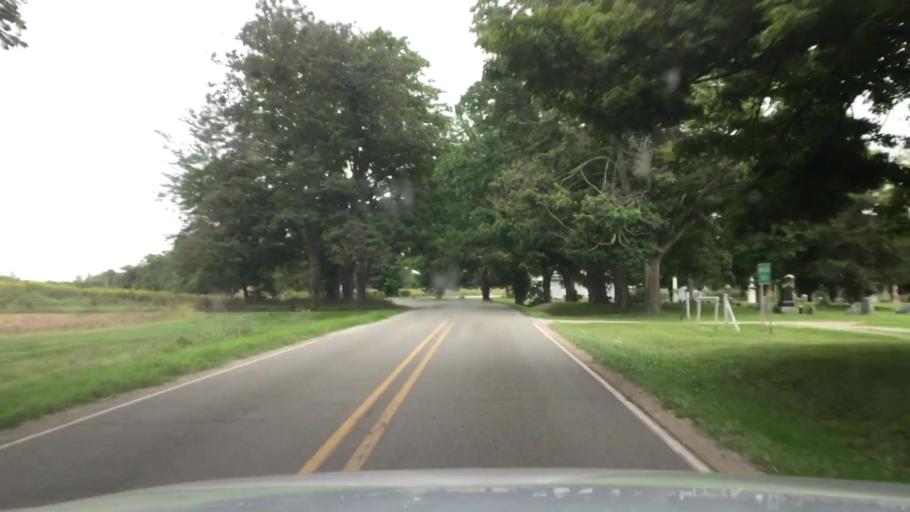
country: US
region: Michigan
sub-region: Shiawassee County
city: Durand
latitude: 42.8280
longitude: -84.0127
